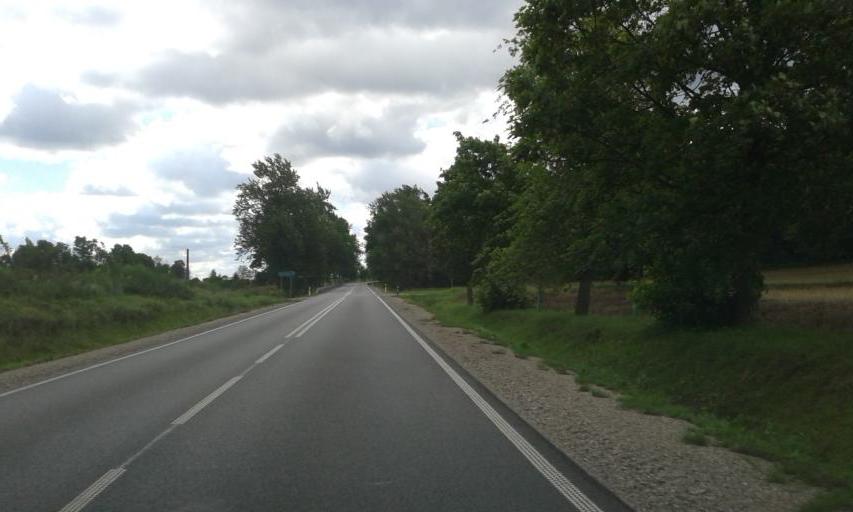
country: PL
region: West Pomeranian Voivodeship
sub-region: Powiat szczecinecki
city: Lubowo
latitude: 53.5068
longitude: 16.3244
